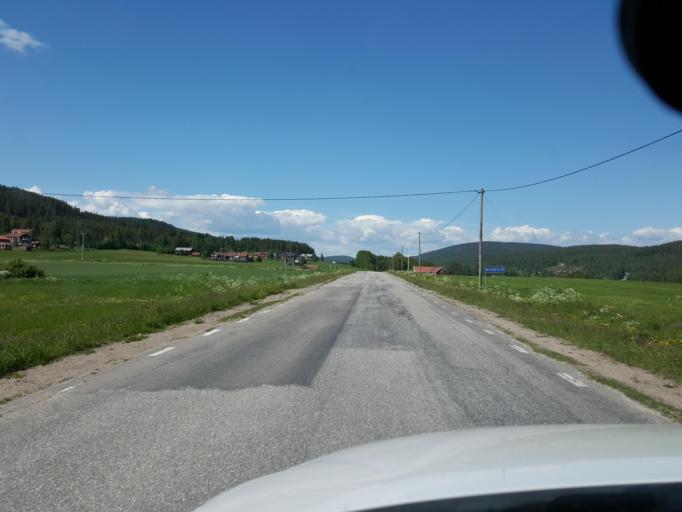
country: SE
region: Gaevleborg
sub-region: Ljusdals Kommun
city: Jaervsoe
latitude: 61.7008
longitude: 16.3014
